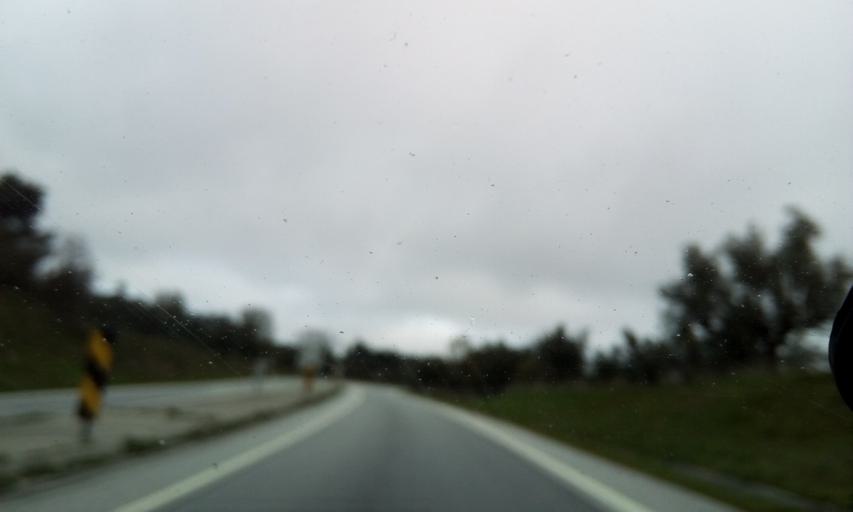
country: PT
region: Guarda
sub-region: Fornos de Algodres
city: Fornos de Algodres
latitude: 40.6279
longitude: -7.5039
